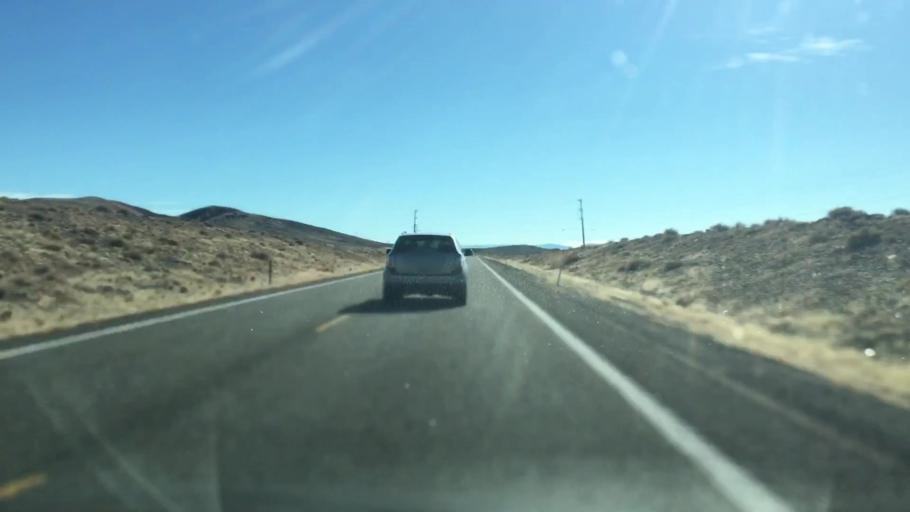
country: US
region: Nevada
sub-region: Lyon County
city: Silver Springs
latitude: 39.1988
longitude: -119.2131
